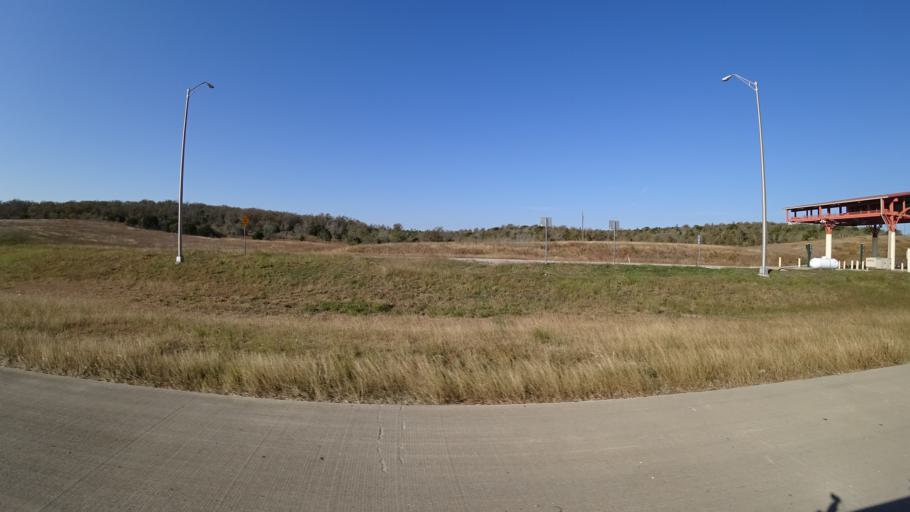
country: US
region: Texas
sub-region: Travis County
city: Manor
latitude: 30.3063
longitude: -97.5697
